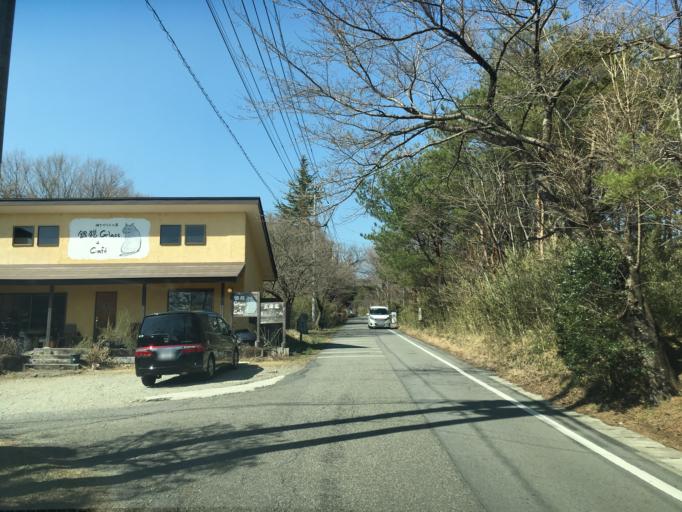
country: JP
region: Tochigi
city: Kuroiso
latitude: 37.0638
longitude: 140.0047
